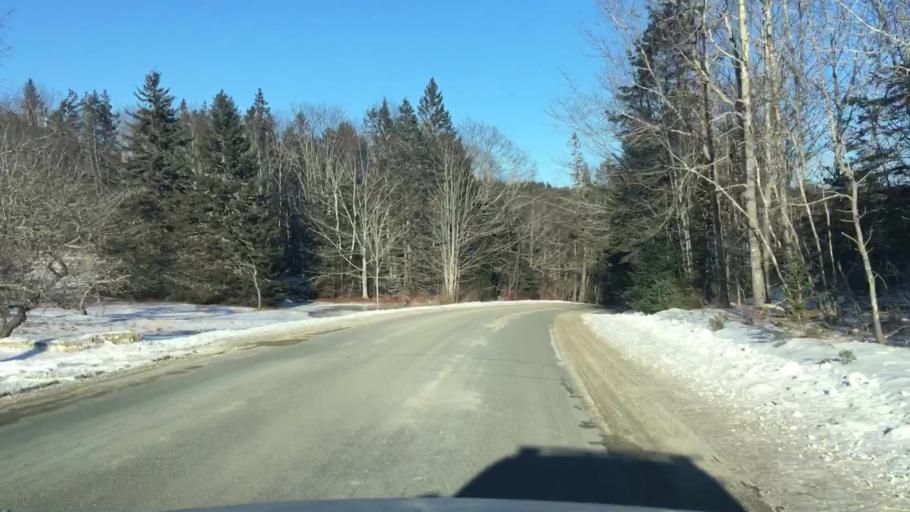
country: US
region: Maine
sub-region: Hancock County
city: Castine
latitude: 44.3595
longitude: -68.7602
